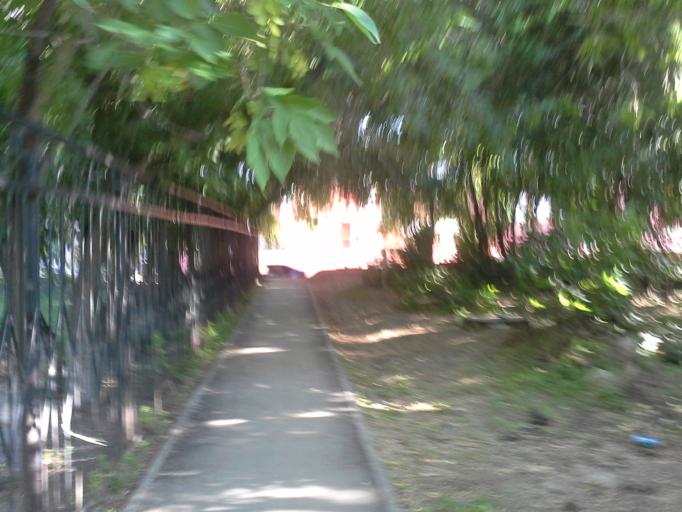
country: RU
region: Novosibirsk
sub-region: Novosibirskiy Rayon
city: Novosibirsk
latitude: 54.9846
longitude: 82.9086
